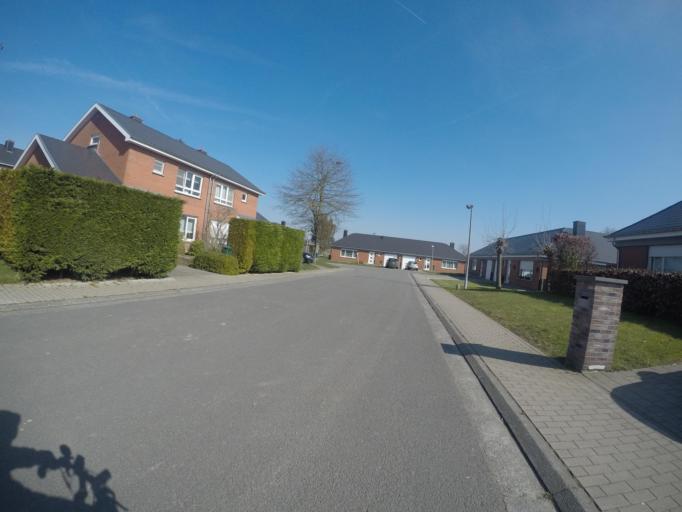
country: BE
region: Flanders
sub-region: Provincie Oost-Vlaanderen
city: Sint-Maria-Lierde
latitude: 50.7881
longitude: 3.8426
